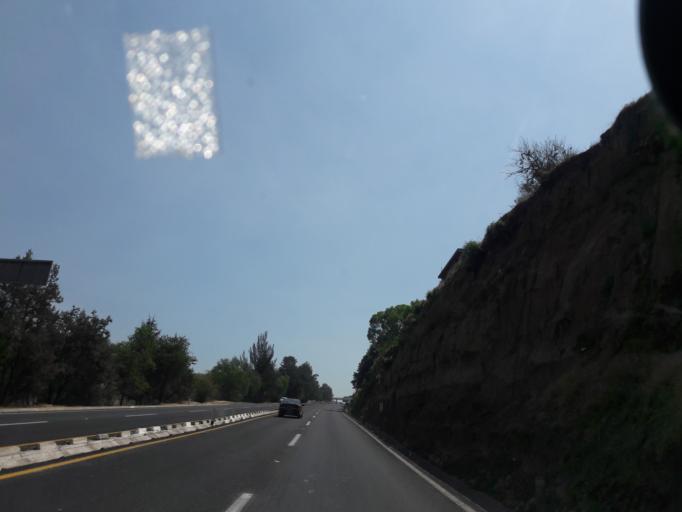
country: MX
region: Tlaxcala
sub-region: Totolac
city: La Trinidad Chimalpa
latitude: 19.3306
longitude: -98.2410
